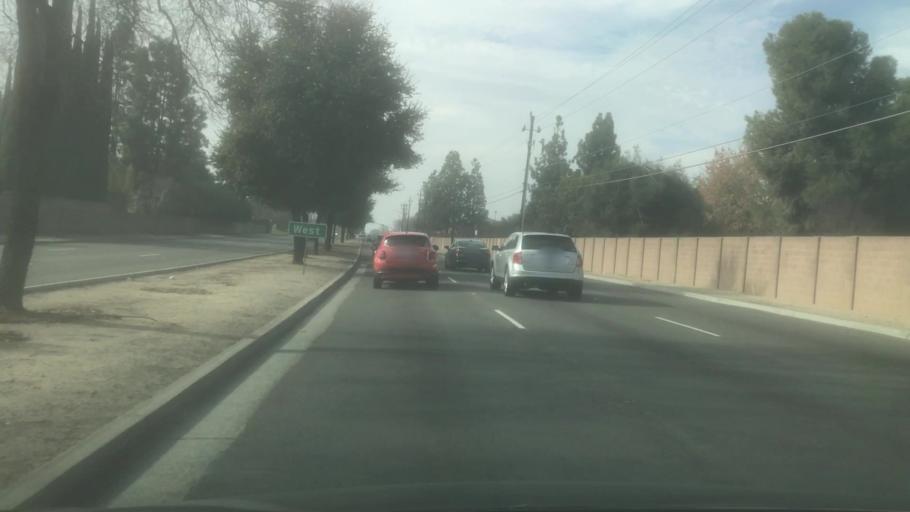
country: US
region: California
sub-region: Fresno County
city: Fresno
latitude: 36.8373
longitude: -119.8221
